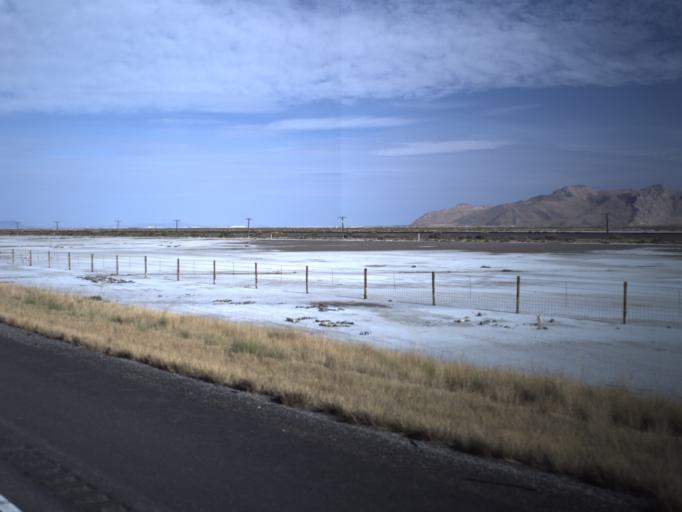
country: US
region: Utah
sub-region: Tooele County
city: Grantsville
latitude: 40.6961
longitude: -112.4752
